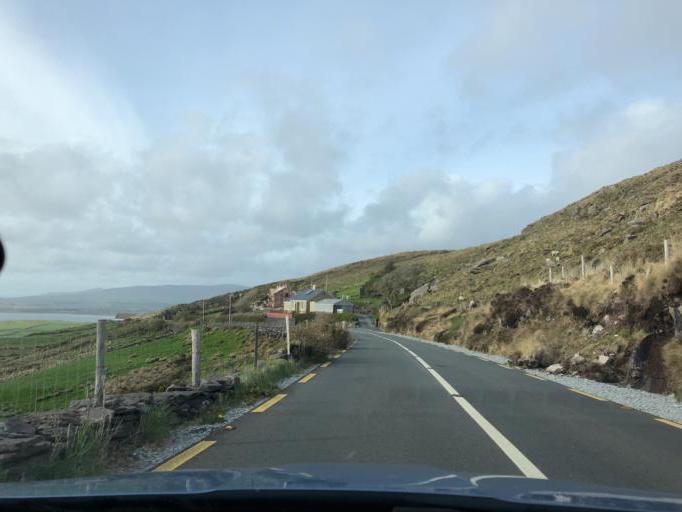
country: IE
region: Munster
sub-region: Ciarrai
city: Cahersiveen
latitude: 51.7955
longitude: -10.1669
